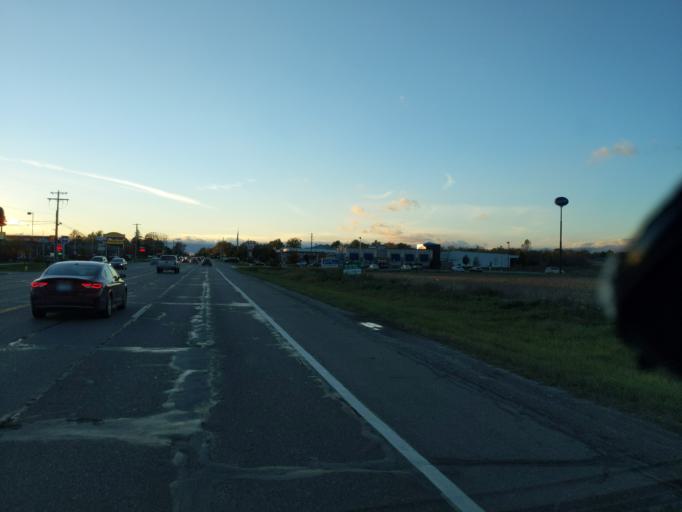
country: US
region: Michigan
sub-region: Eaton County
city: Waverly
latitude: 42.7411
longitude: -84.6757
